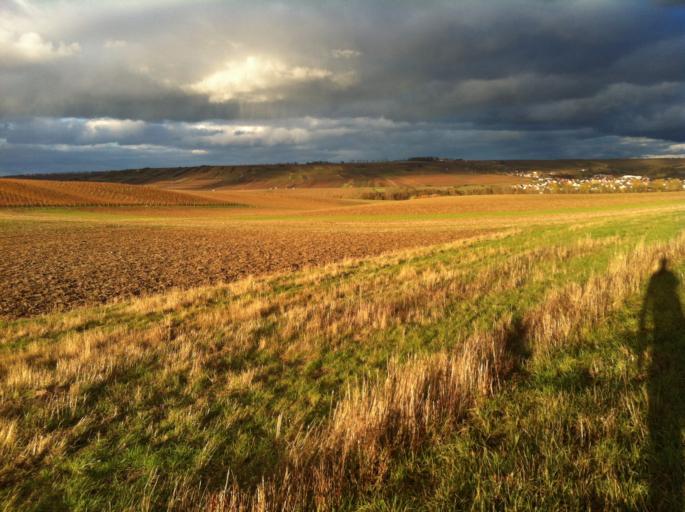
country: DE
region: Rheinland-Pfalz
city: Jugenheim
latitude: 49.9048
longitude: 8.1038
